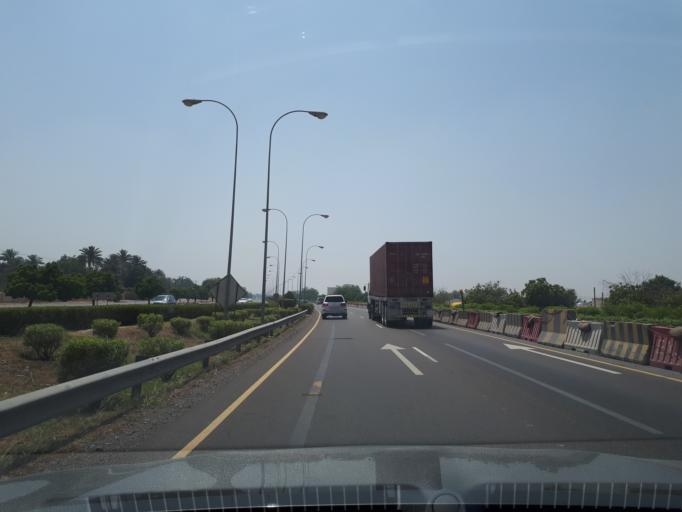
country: OM
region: Al Batinah
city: Al Sohar
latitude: 24.3930
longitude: 56.6923
